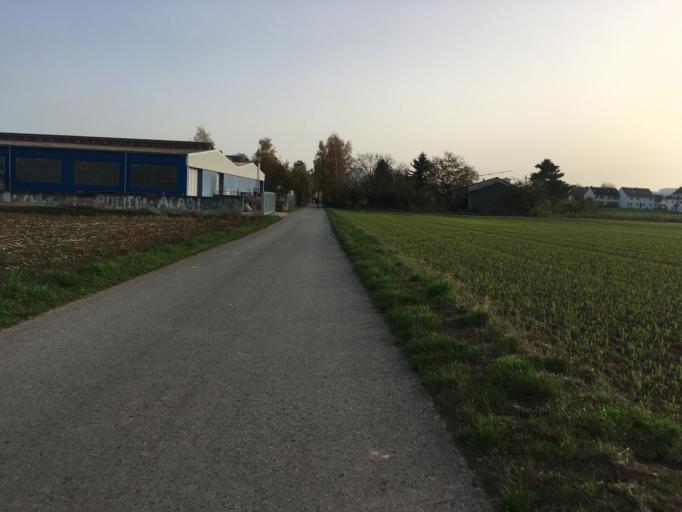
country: DE
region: Baden-Wuerttemberg
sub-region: Regierungsbezirk Stuttgart
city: Bonnigheim
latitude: 49.0463
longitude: 9.0897
